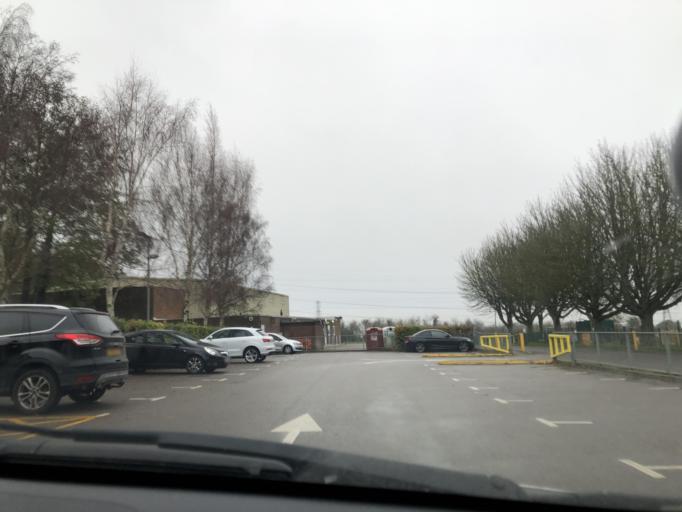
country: GB
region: England
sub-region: Kent
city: Gravesend
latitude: 51.4080
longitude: 0.3515
